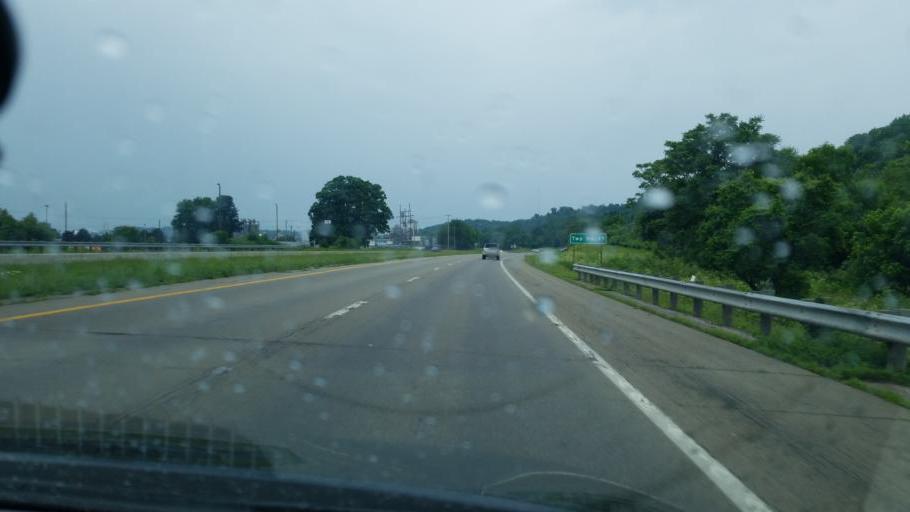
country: US
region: West Virginia
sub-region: Wood County
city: Blennerhassett
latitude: 39.2827
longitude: -81.6292
